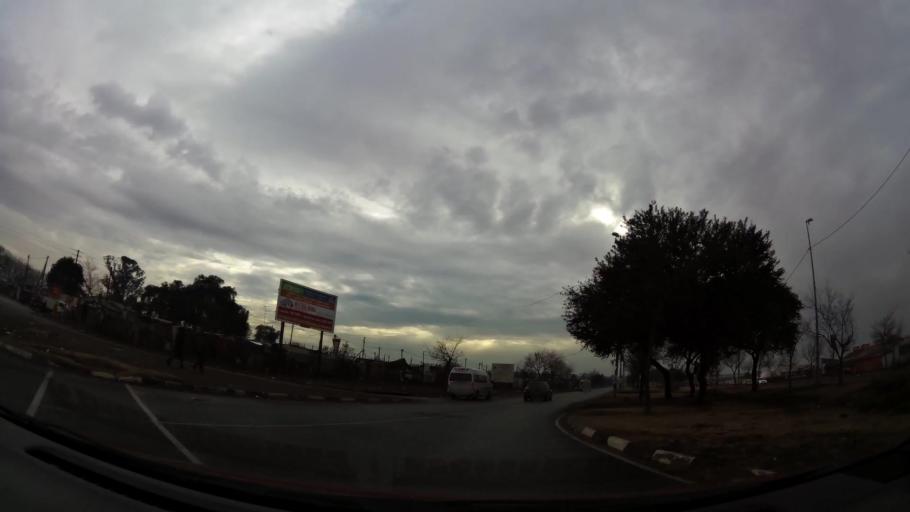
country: ZA
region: Gauteng
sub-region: City of Johannesburg Metropolitan Municipality
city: Soweto
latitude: -26.2903
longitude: 27.8444
